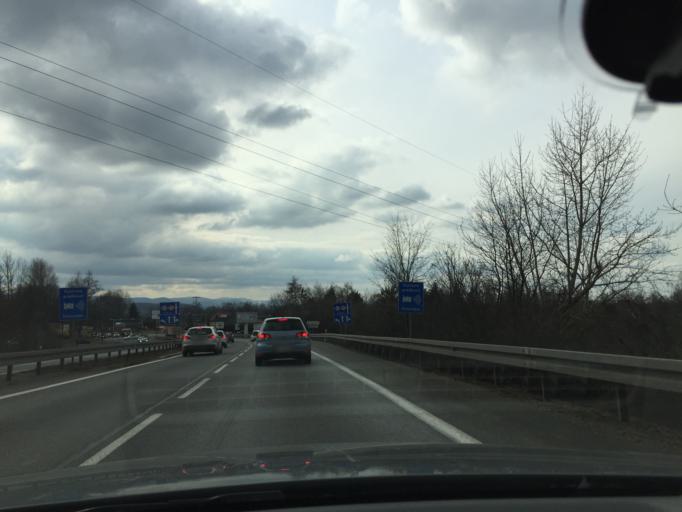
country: PL
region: Silesian Voivodeship
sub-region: Powiat bielski
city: Czechowice-Dziedzice
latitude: 49.9202
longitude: 18.9899
